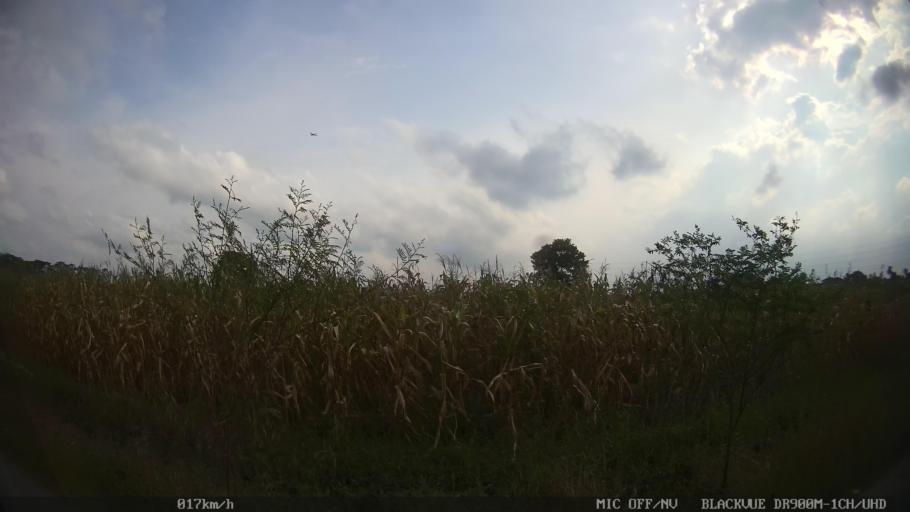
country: ID
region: North Sumatra
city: Percut
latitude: 3.5667
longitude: 98.7862
